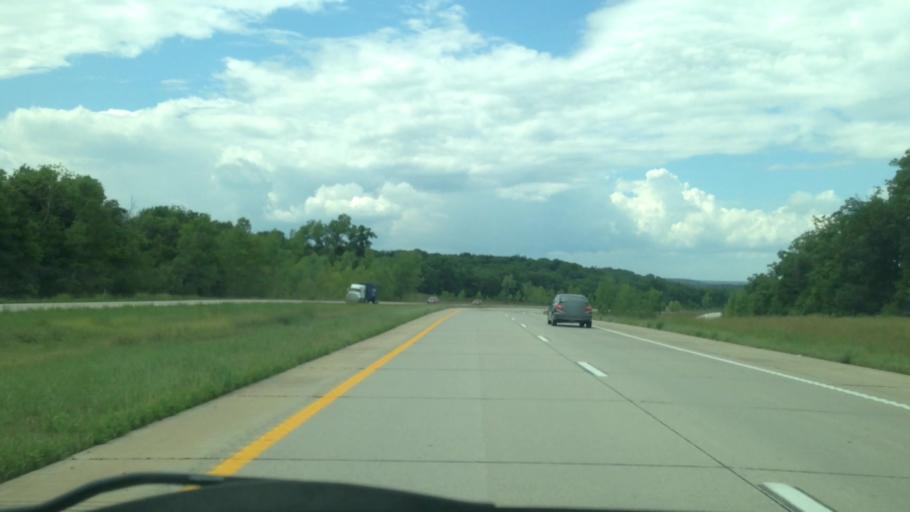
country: US
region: Missouri
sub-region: Pike County
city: Bowling Green
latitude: 39.3956
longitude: -91.2395
